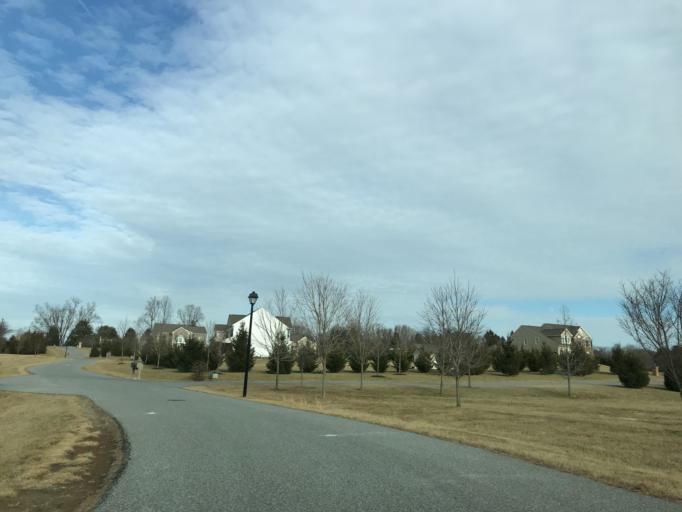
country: US
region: Maryland
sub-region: Baltimore County
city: Kingsville
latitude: 39.4483
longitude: -76.4076
